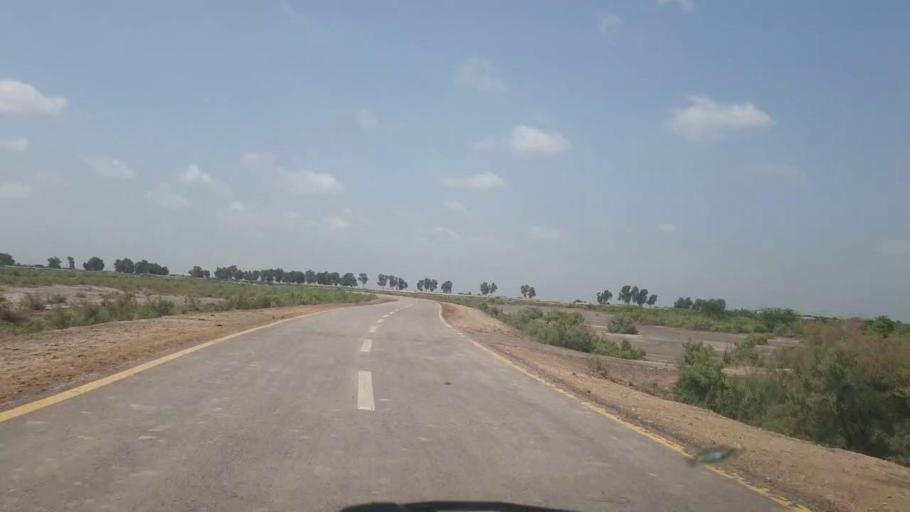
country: PK
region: Sindh
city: Berani
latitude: 25.7061
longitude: 68.9413
